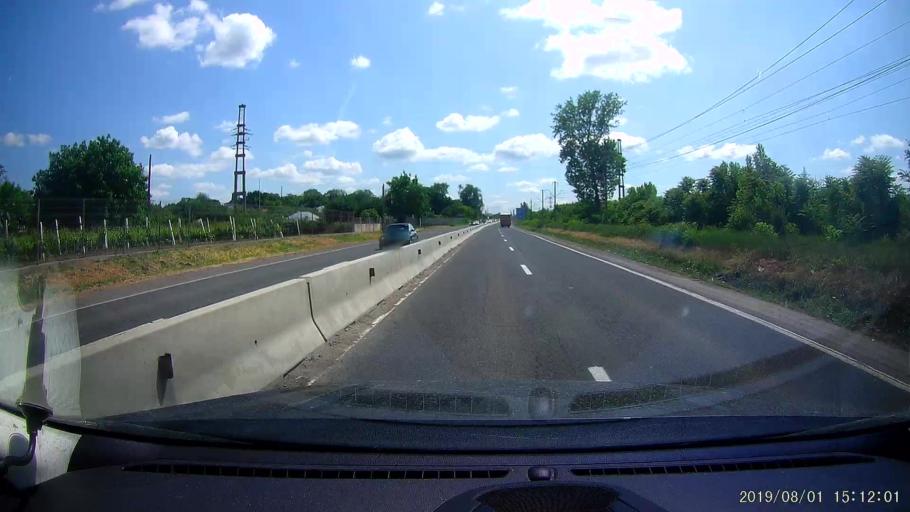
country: RO
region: Braila
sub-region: Comuna Chiscani
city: Lacu Sarat
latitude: 45.2108
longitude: 27.9179
